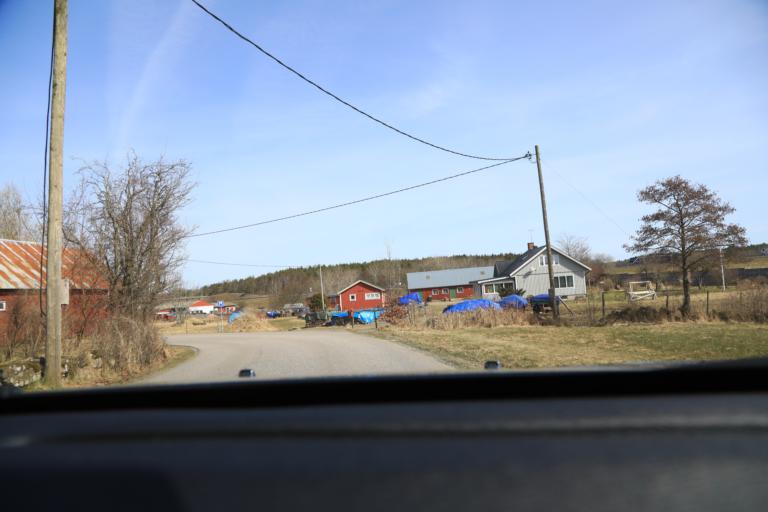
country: SE
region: Halland
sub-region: Kungsbacka Kommun
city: Frillesas
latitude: 57.2461
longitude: 12.2162
